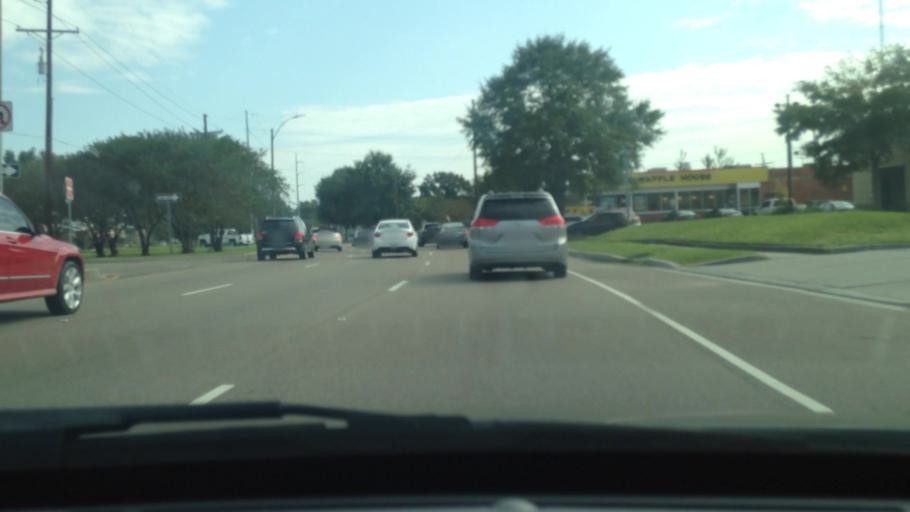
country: US
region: Louisiana
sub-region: Jefferson Parish
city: Terrytown
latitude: 29.9290
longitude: -90.0321
